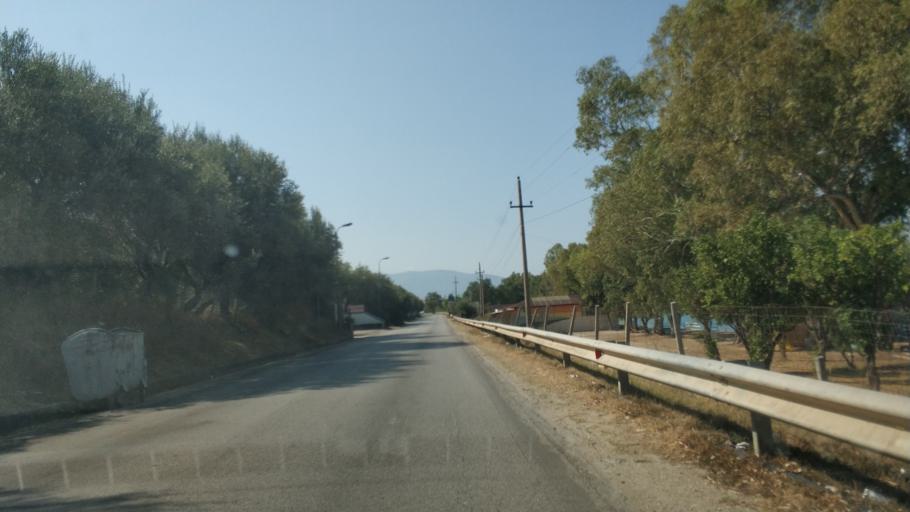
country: AL
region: Vlore
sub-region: Rrethi i Vlores
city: Orikum
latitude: 40.3813
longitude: 19.4836
